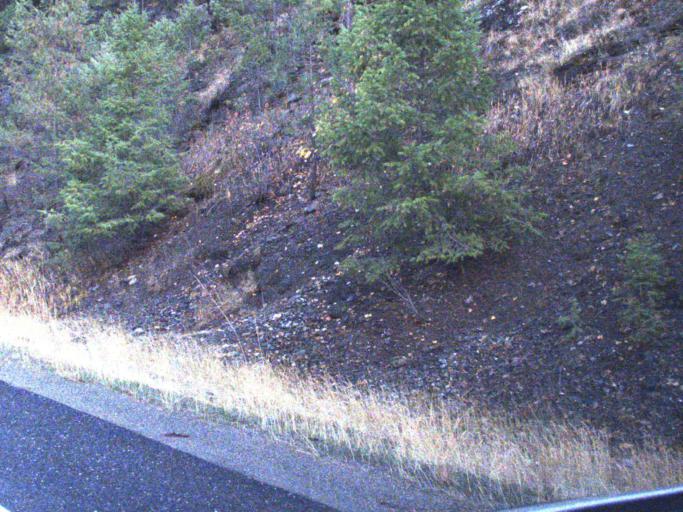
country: US
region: Washington
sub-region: Stevens County
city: Kettle Falls
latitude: 48.6721
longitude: -118.0289
